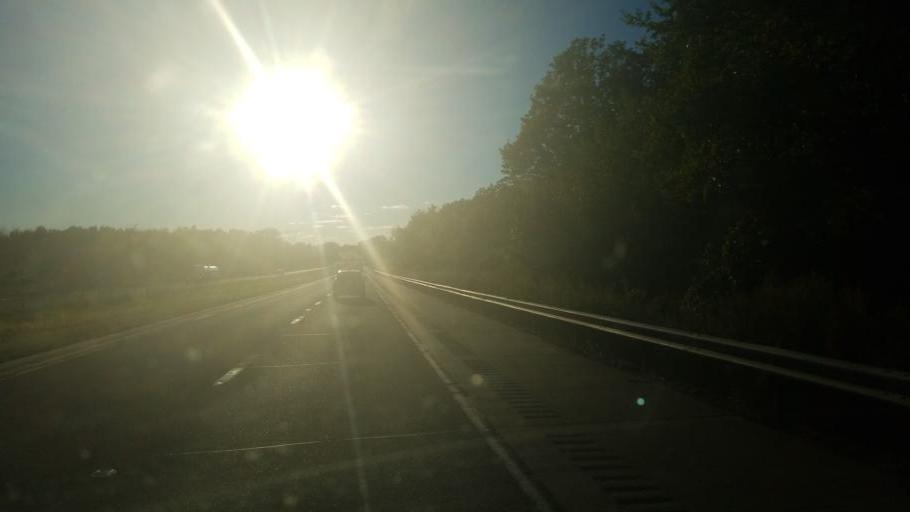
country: US
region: Pennsylvania
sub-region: Erie County
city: Fairview
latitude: 42.0219
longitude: -80.1616
